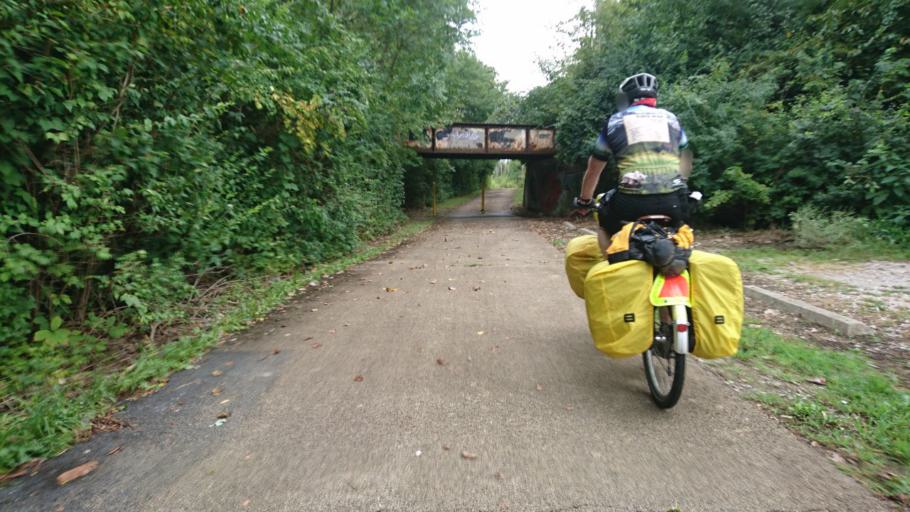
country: US
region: Illinois
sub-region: Sangamon County
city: Southern View
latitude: 39.7580
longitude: -89.6680
